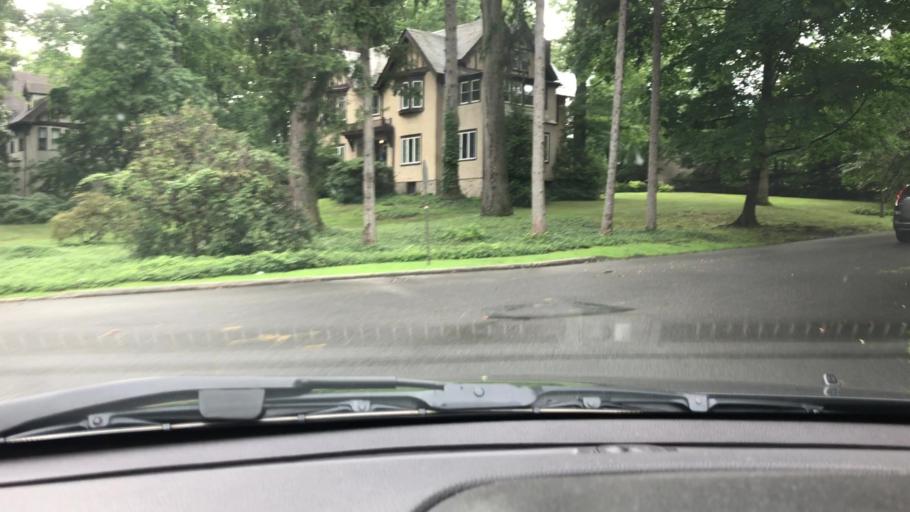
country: US
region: New York
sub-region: Westchester County
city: New Rochelle
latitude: 40.9311
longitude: -73.7843
